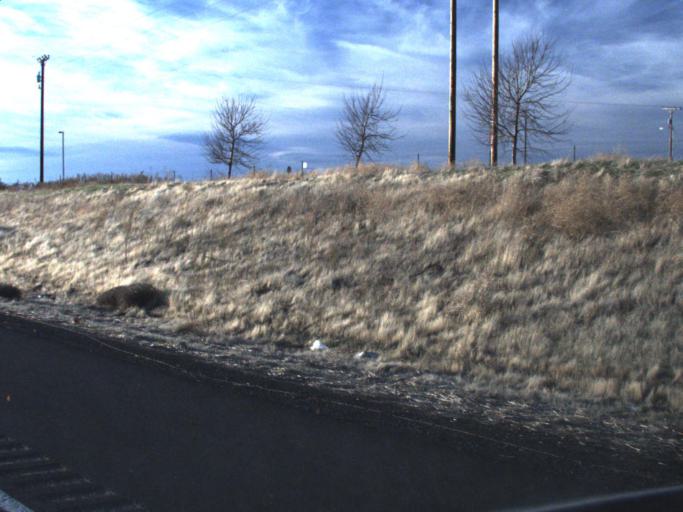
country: US
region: Washington
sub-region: Walla Walla County
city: Garrett
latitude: 46.0718
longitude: -118.4087
